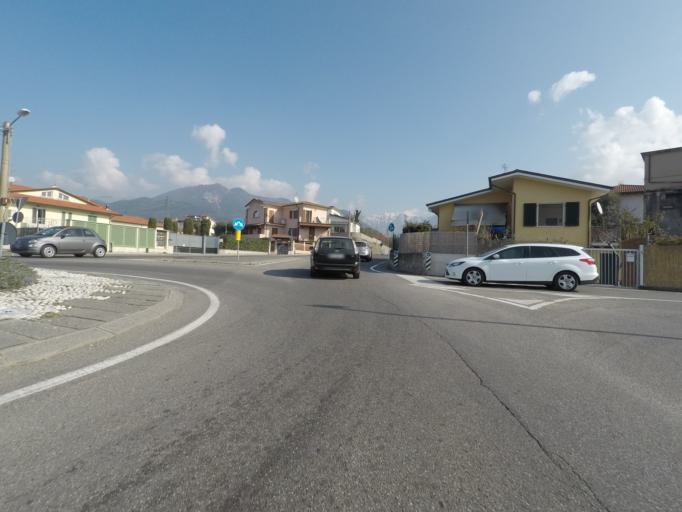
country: IT
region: Tuscany
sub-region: Provincia di Massa-Carrara
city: Massa
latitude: 44.0262
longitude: 10.1258
